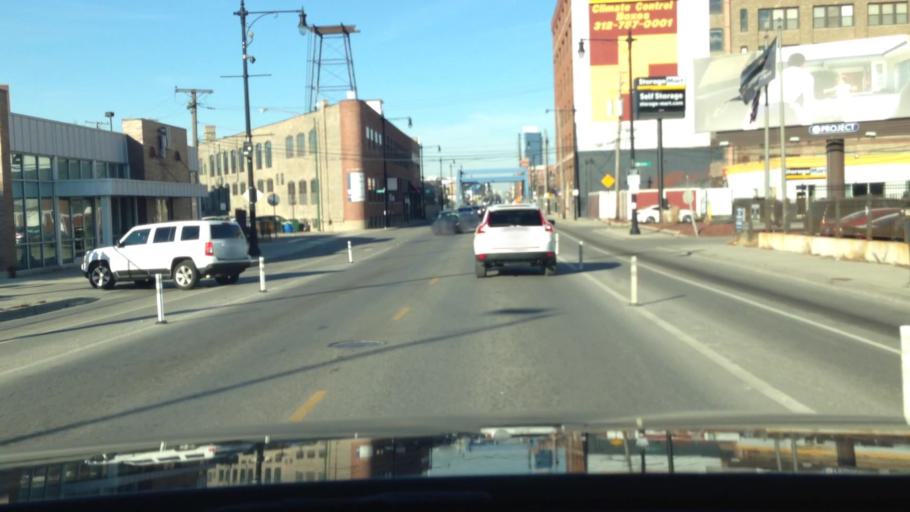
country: US
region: Illinois
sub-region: Cook County
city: Chicago
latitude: 41.8996
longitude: -87.6479
